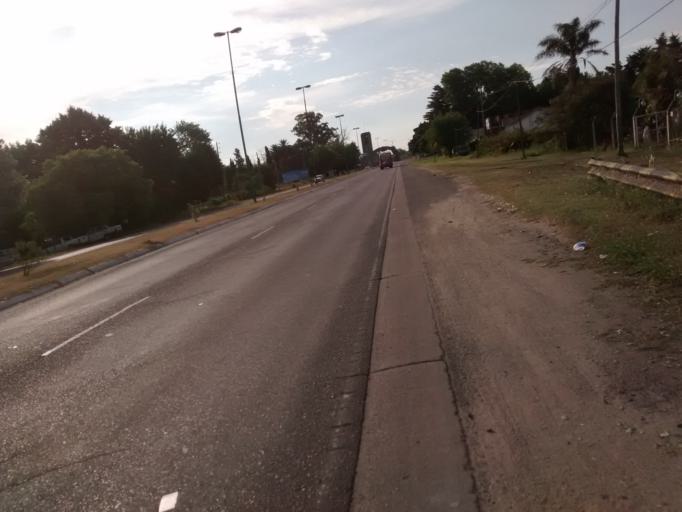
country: AR
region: Buenos Aires
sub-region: Partido de La Plata
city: La Plata
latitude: -34.8490
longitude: -58.0958
